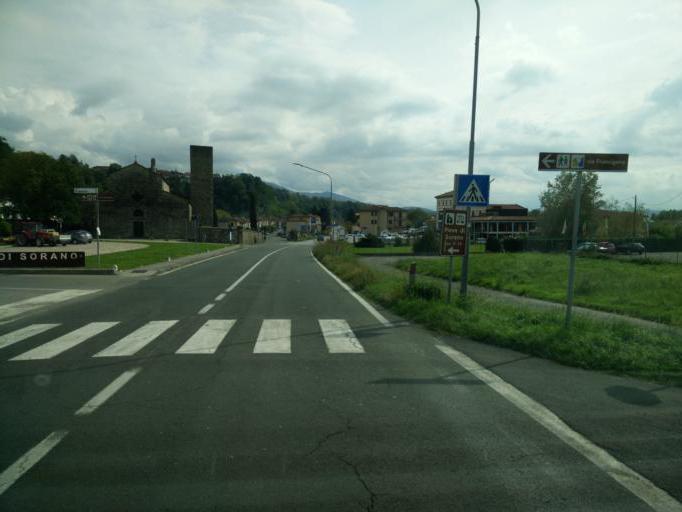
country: IT
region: Tuscany
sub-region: Provincia di Massa-Carrara
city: Filattiera
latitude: 44.3327
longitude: 9.9283
